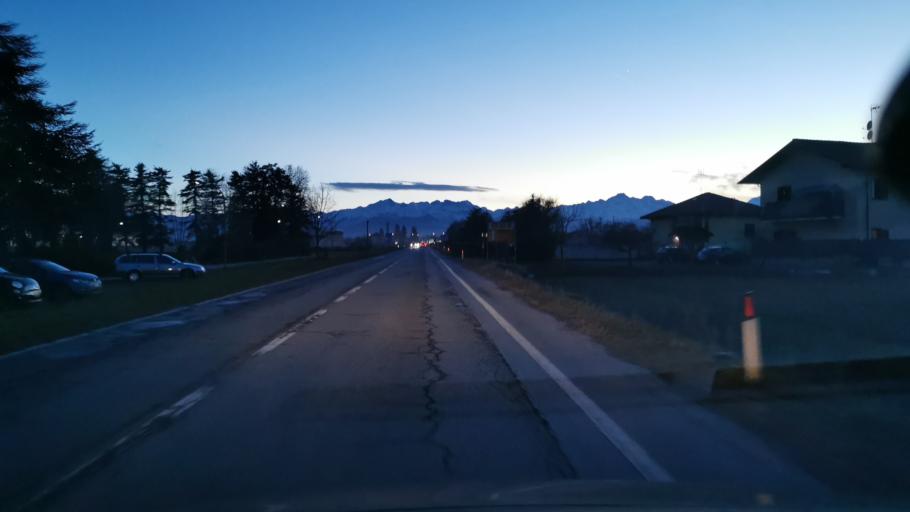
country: IT
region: Piedmont
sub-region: Provincia di Cuneo
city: Roata Rossi
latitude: 44.4385
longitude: 7.5627
